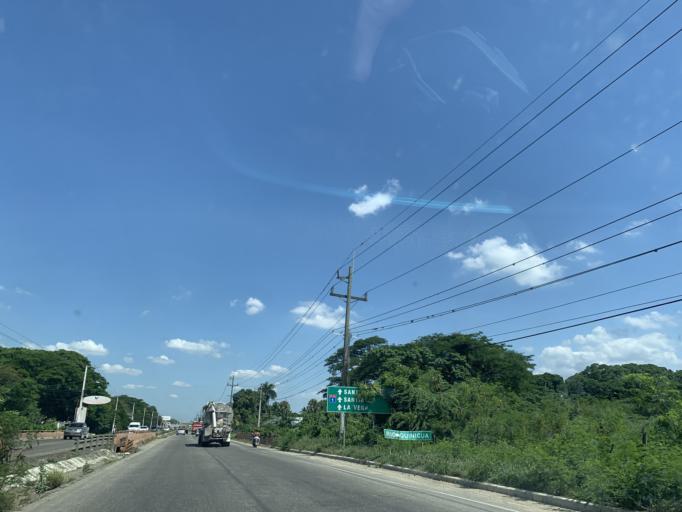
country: DO
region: Santiago
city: Villa Gonzalez
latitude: 19.5236
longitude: -70.7691
